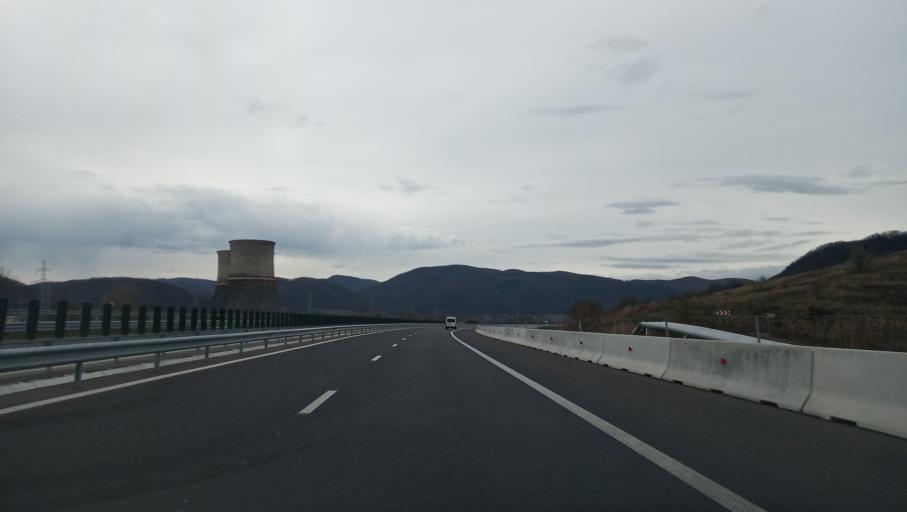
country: RO
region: Hunedoara
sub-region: Comuna Vetel
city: Vetel
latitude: 45.9225
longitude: 22.8263
